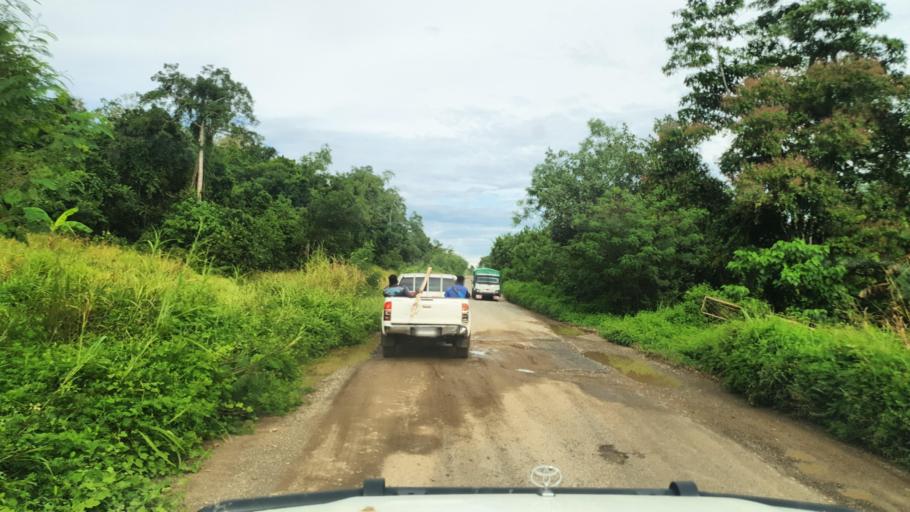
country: PG
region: Gulf
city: Kerema
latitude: -8.3436
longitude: 146.3327
